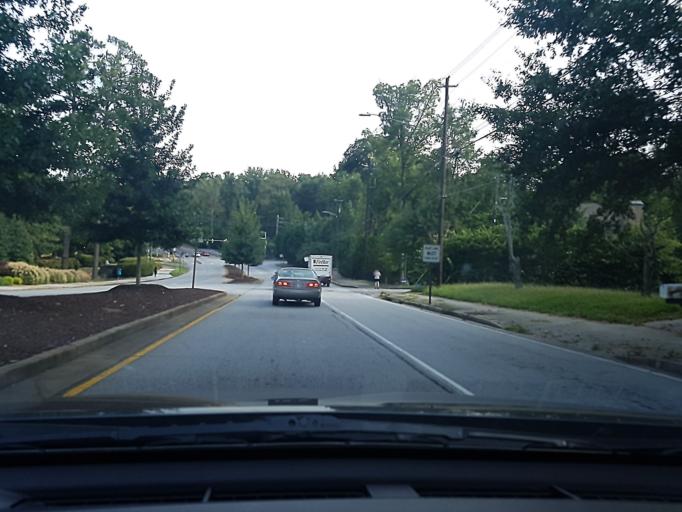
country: US
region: Georgia
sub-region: DeKalb County
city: North Atlanta
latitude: 33.8467
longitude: -84.3488
